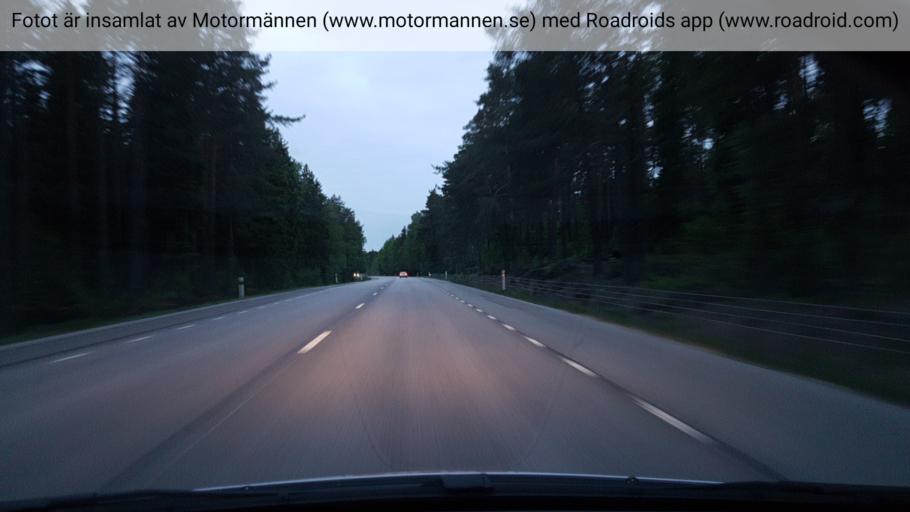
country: SE
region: Uppsala
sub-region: Heby Kommun
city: Heby
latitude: 59.9393
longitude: 16.7733
